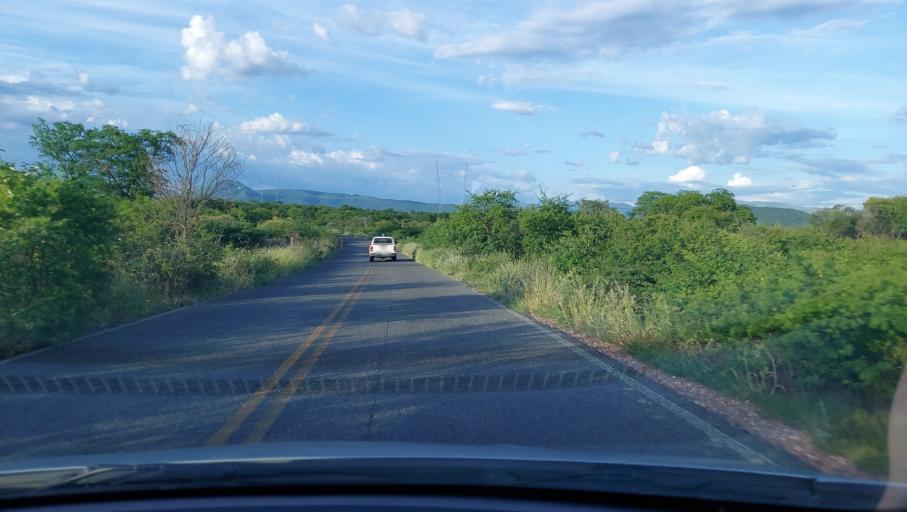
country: BR
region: Bahia
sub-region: Oliveira Dos Brejinhos
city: Beira Rio
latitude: -12.1960
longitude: -42.5377
